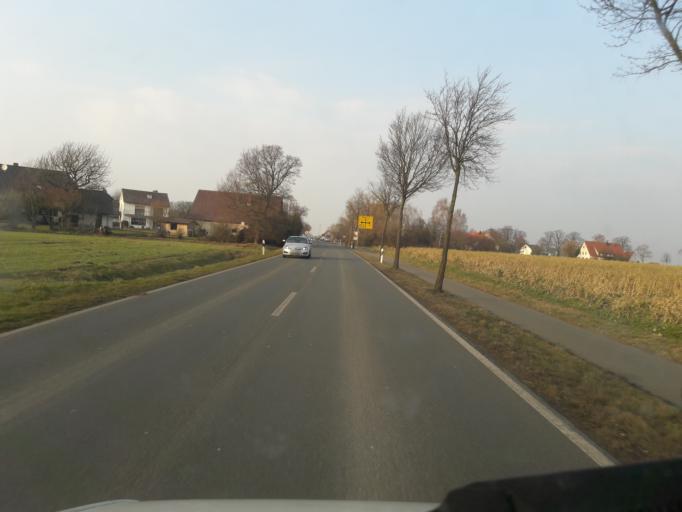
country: DE
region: North Rhine-Westphalia
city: Espelkamp
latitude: 52.3462
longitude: 8.6501
